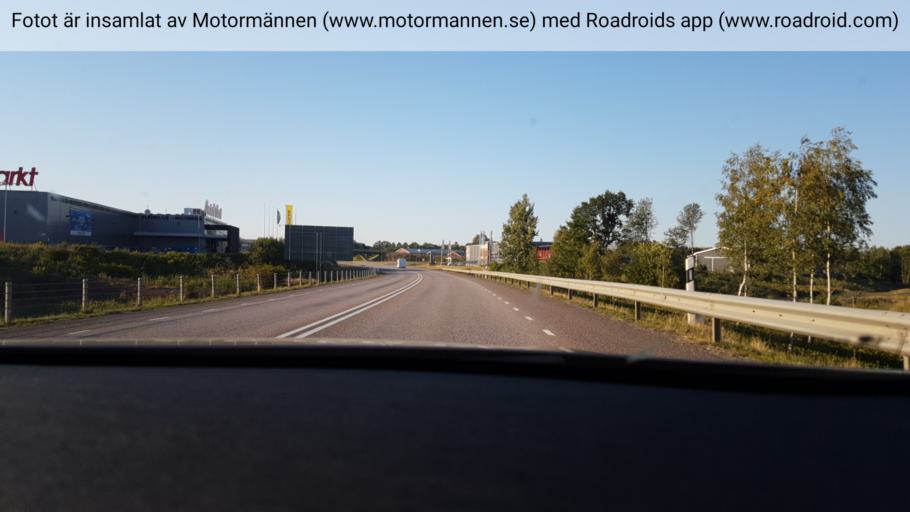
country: SE
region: Vaestra Goetaland
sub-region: Skovde Kommun
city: Skoevde
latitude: 58.4092
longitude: 13.8789
